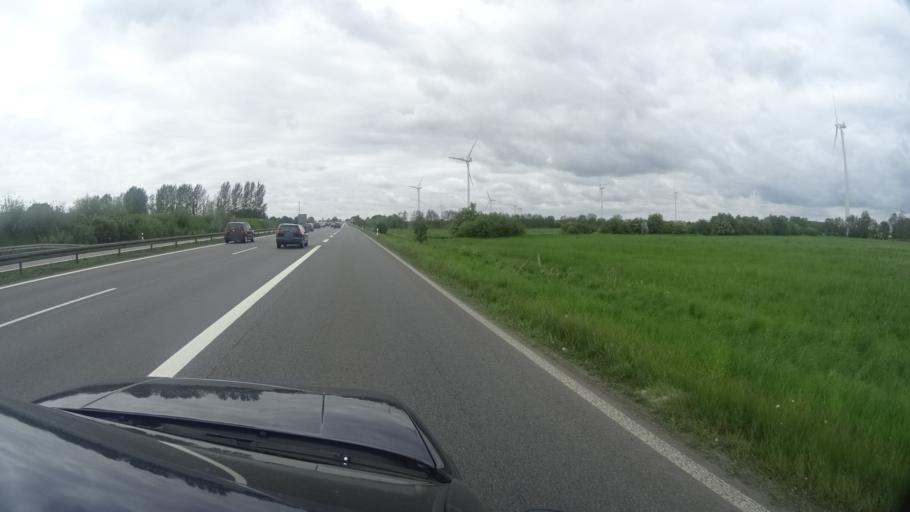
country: DE
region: Brandenburg
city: Dabergotz
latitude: 52.9082
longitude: 12.7353
